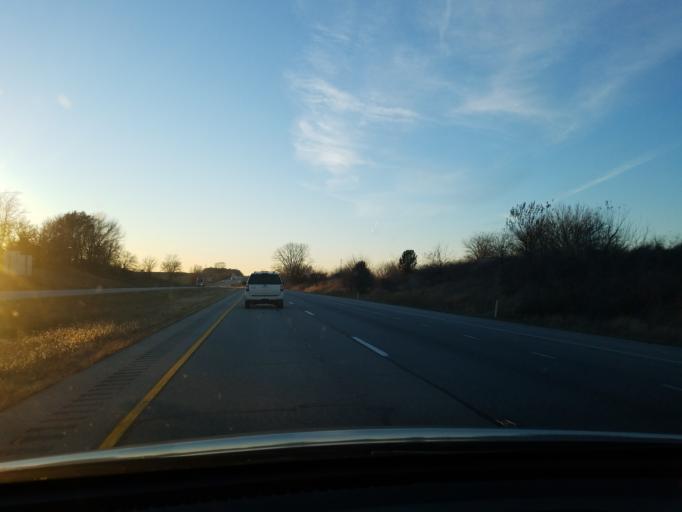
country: US
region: Indiana
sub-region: Posey County
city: Poseyville
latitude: 38.1842
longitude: -87.7878
